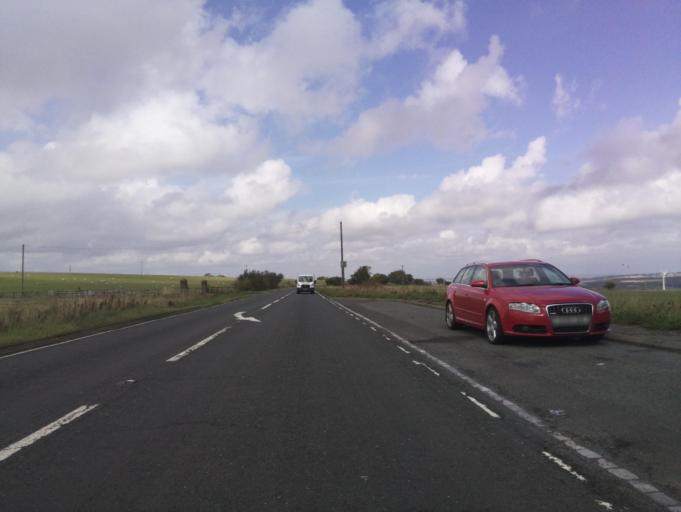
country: GB
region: England
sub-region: County Durham
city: Castleside
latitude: 54.8127
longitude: -1.8628
